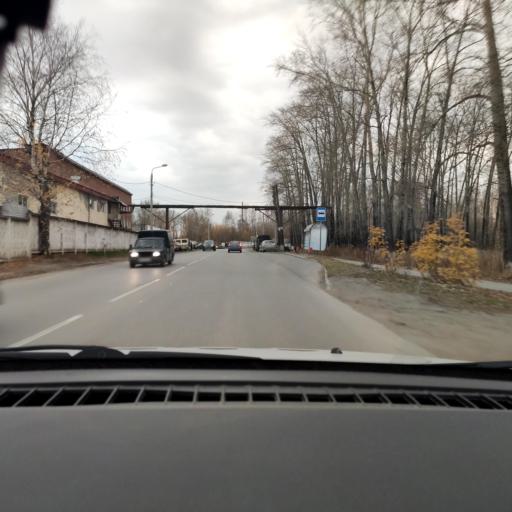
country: RU
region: Perm
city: Polazna
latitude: 58.1210
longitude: 56.3889
